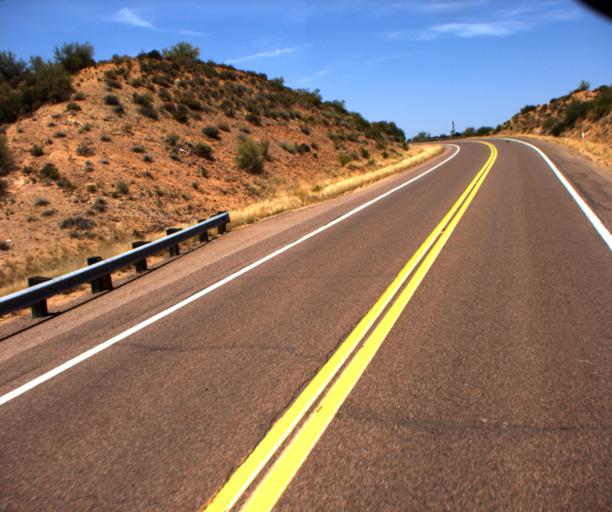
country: US
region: Arizona
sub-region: Gila County
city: Tonto Basin
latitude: 33.7028
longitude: -111.1898
